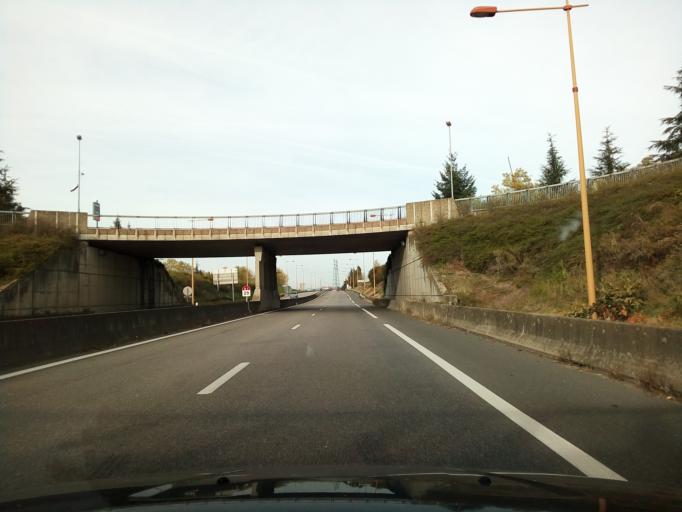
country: FR
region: Rhone-Alpes
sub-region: Departement de la Loire
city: Mably
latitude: 46.0630
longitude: 4.0624
